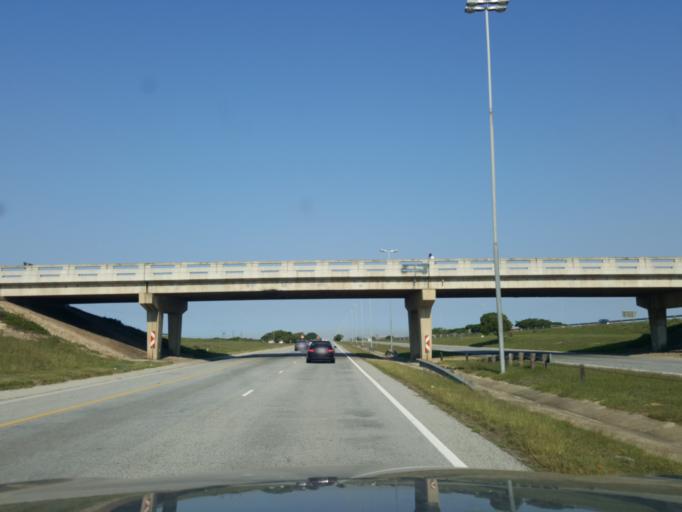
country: ZA
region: Eastern Cape
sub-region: Nelson Mandela Bay Metropolitan Municipality
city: Port Elizabeth
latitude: -33.8225
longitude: 25.6474
